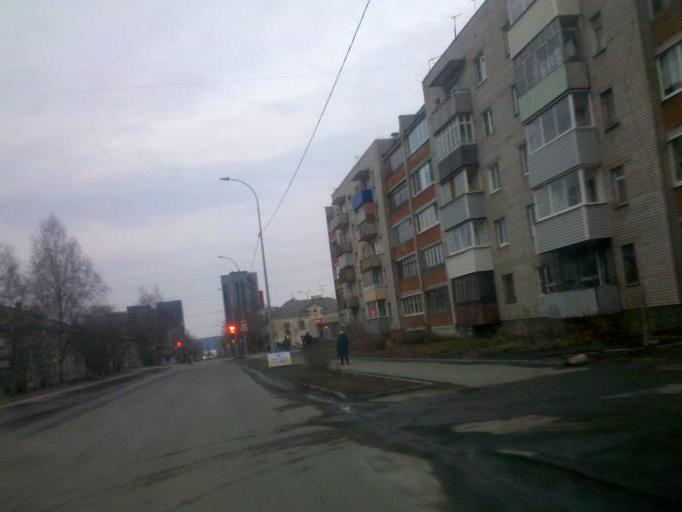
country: RU
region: Republic of Karelia
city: Petrozavodsk
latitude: 61.8023
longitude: 34.3337
